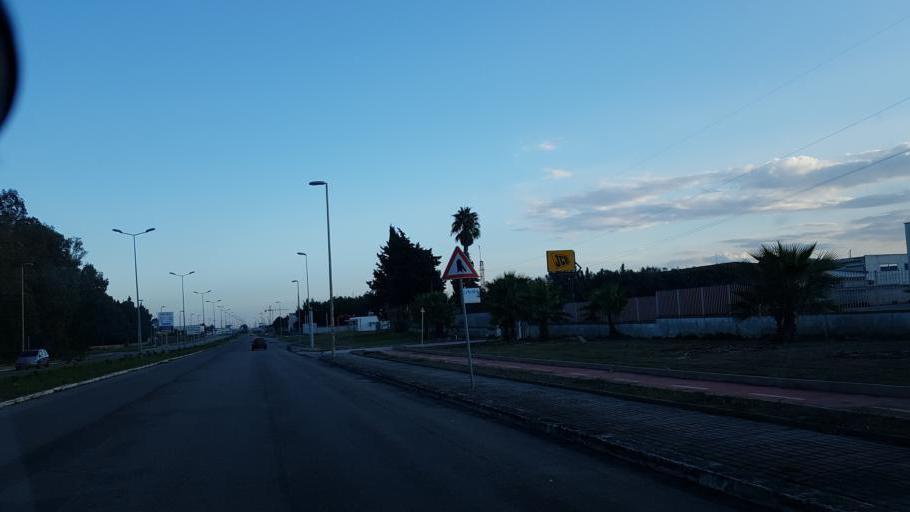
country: IT
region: Apulia
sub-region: Provincia di Lecce
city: Surbo
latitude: 40.3827
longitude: 18.1207
